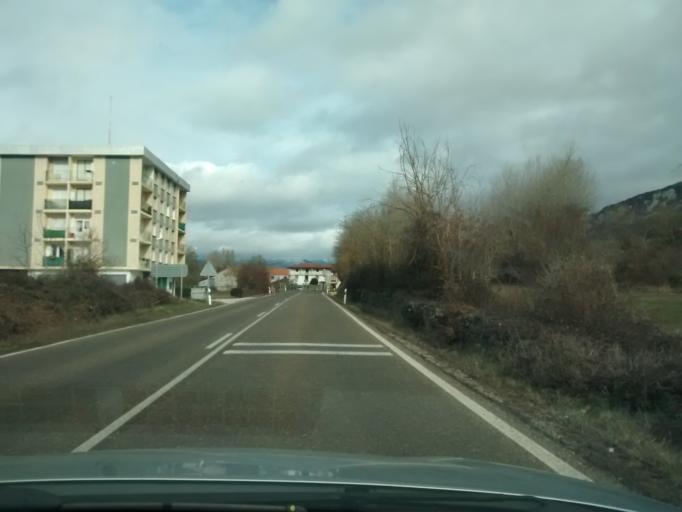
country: ES
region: Castille and Leon
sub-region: Provincia de Burgos
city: Espinosa de los Monteros
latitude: 43.0236
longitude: -3.4842
